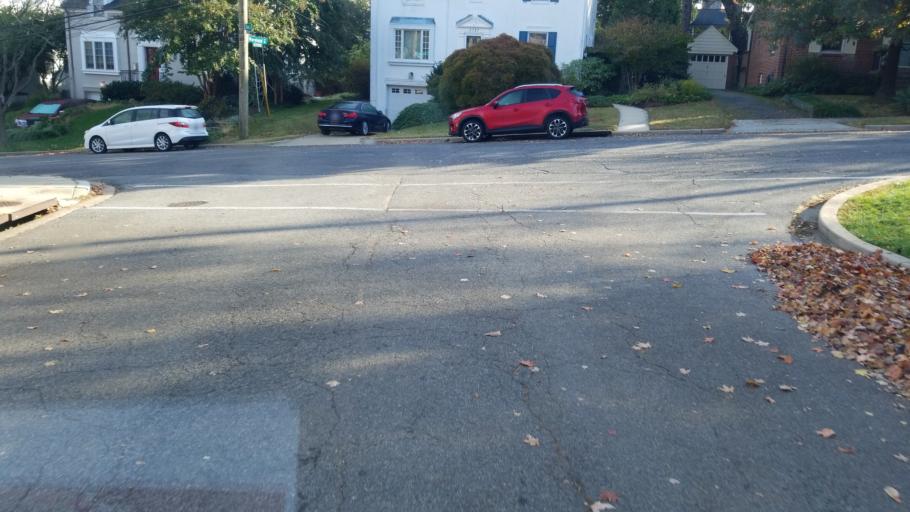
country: US
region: Maryland
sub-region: Montgomery County
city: Chevy Chase
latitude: 38.9680
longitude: -77.0574
